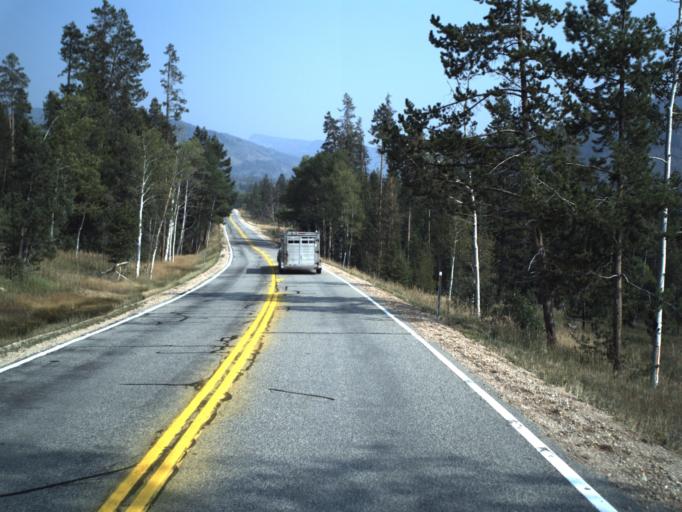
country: US
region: Utah
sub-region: Summit County
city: Francis
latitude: 40.6016
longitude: -111.1142
